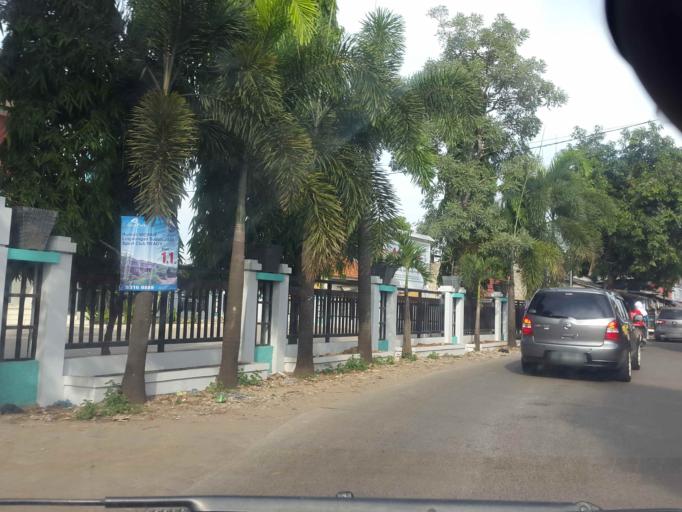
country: ID
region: West Java
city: Serpong
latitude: -6.2789
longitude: 106.6674
